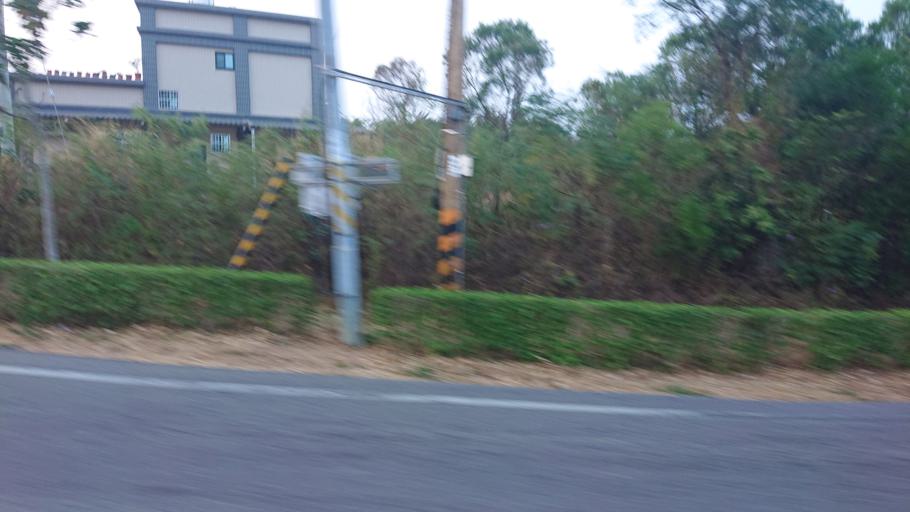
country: TW
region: Fukien
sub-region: Kinmen
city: Jincheng
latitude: 24.4540
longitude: 118.3180
